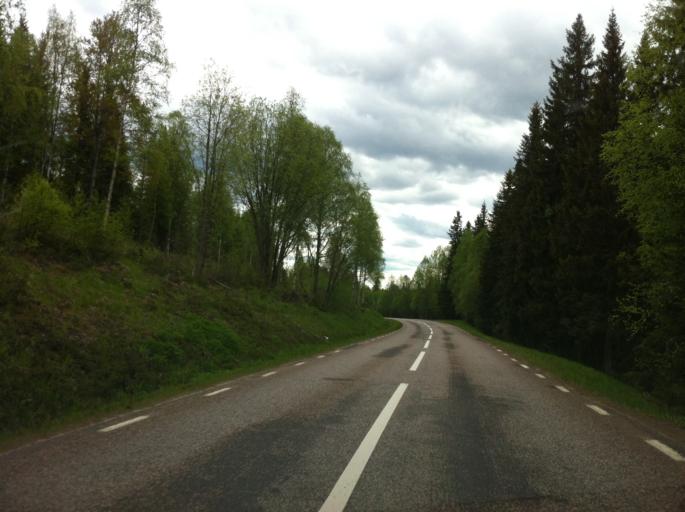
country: SE
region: Dalarna
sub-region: Malung-Saelens kommun
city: Malung
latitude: 61.2189
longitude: 13.2203
